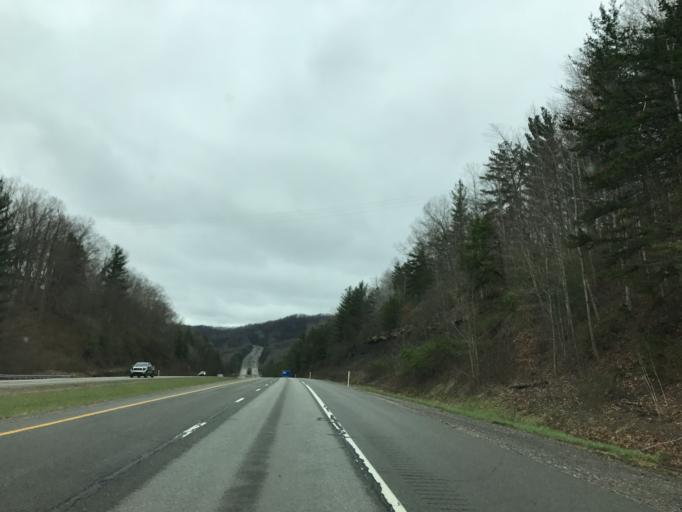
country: US
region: West Virginia
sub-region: Fayette County
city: Mount Hope
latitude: 37.9041
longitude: -81.1744
